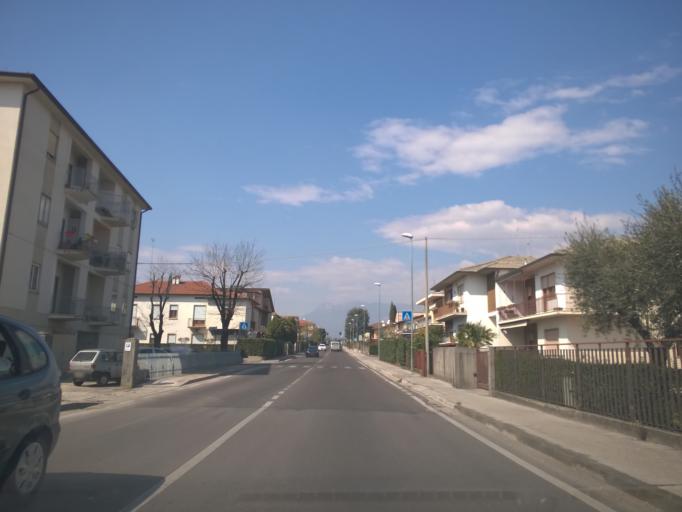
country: IT
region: Veneto
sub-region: Provincia di Vicenza
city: Thiene
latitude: 45.7106
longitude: 11.4929
